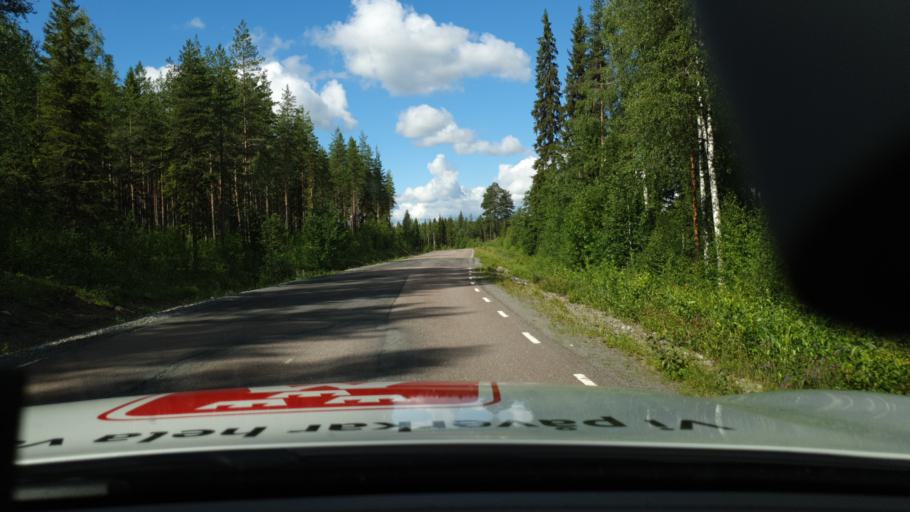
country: SE
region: Norrbotten
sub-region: Bodens Kommun
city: Saevast
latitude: 65.8760
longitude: 21.9094
